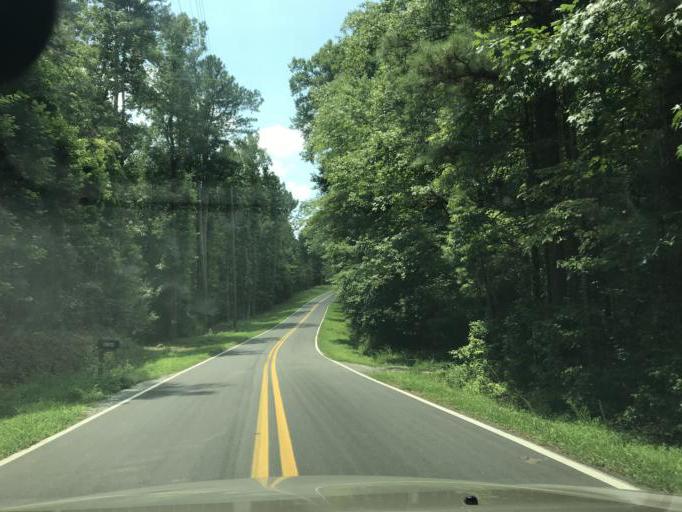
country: US
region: Georgia
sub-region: Dawson County
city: Dawsonville
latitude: 34.3282
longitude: -84.2121
